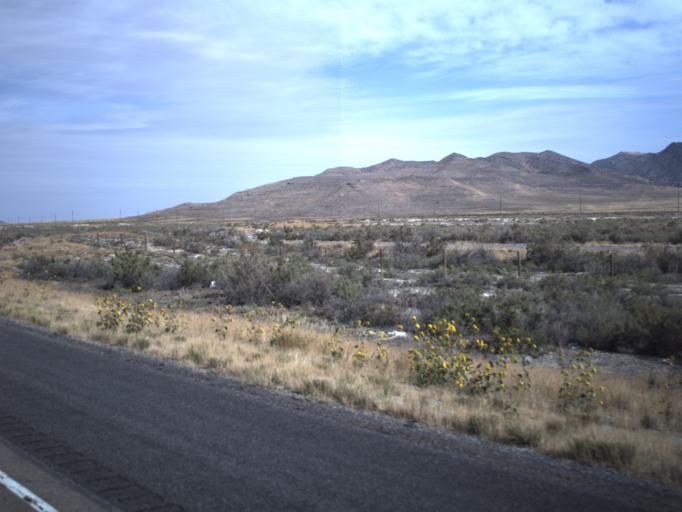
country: US
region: Utah
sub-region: Tooele County
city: Grantsville
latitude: 40.7809
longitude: -112.8141
